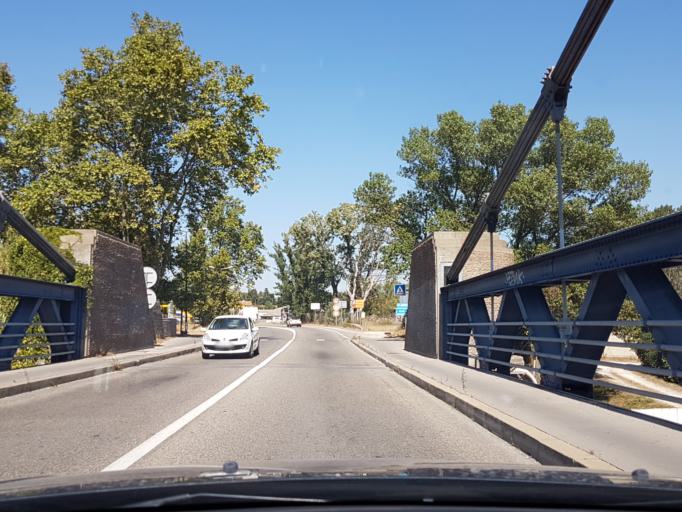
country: FR
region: Provence-Alpes-Cote d'Azur
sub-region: Departement des Bouches-du-Rhone
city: Rognonas
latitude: 43.9161
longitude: 4.8090
